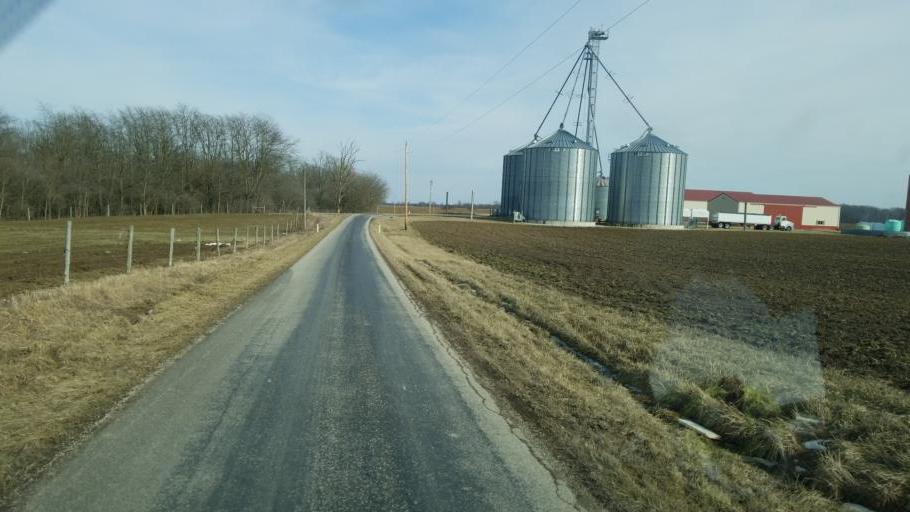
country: US
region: Ohio
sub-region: Union County
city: Richwood
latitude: 40.3659
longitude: -83.2456
